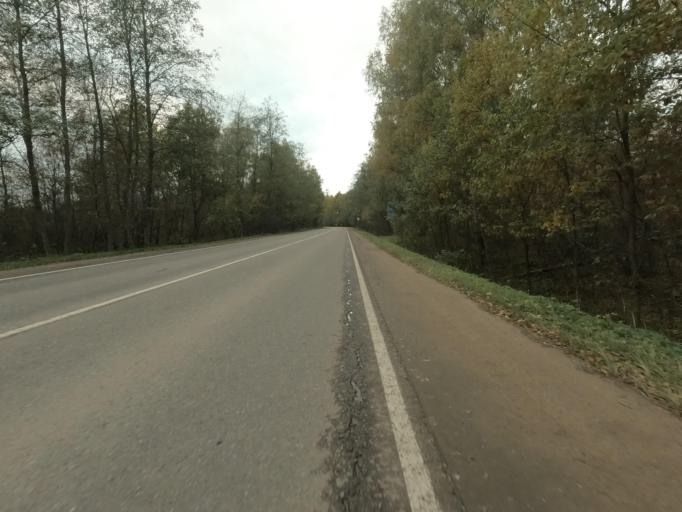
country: RU
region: Leningrad
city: Pavlovo
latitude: 59.7997
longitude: 30.9429
